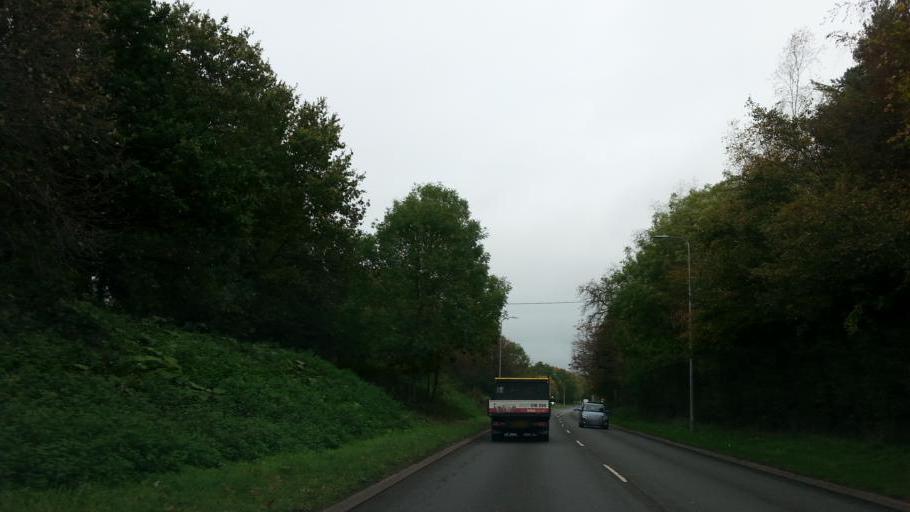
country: GB
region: England
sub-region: Worcestershire
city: Bromsgrove
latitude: 52.3407
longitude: -2.0483
